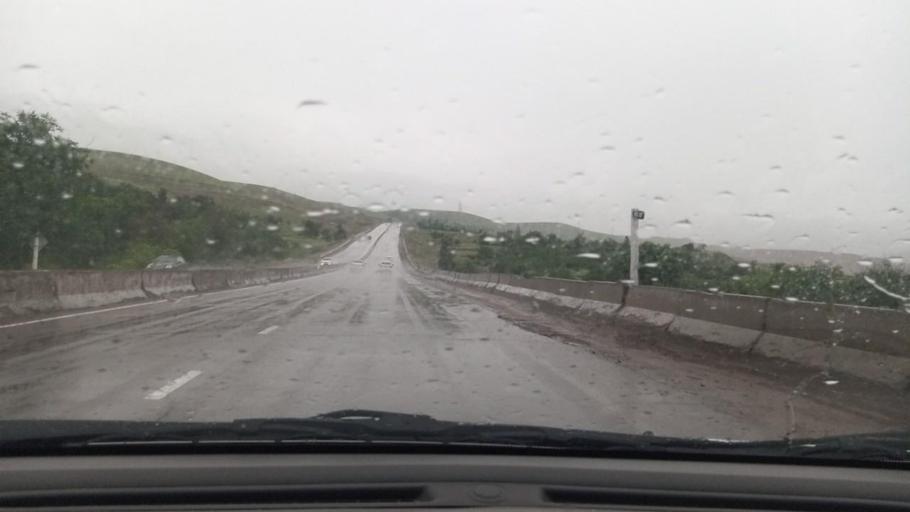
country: UZ
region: Toshkent
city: Angren
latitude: 41.0520
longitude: 70.1609
